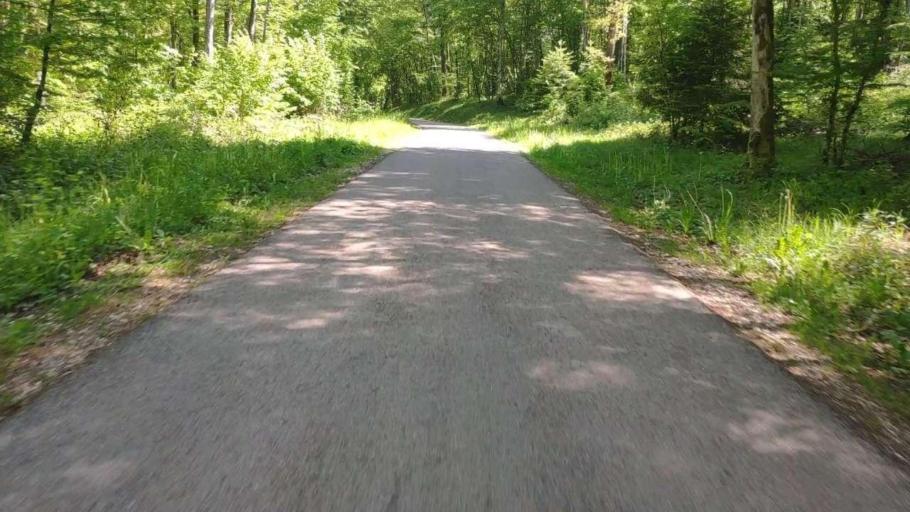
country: FR
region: Franche-Comte
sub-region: Departement du Jura
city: Poligny
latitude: 46.7482
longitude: 5.7763
